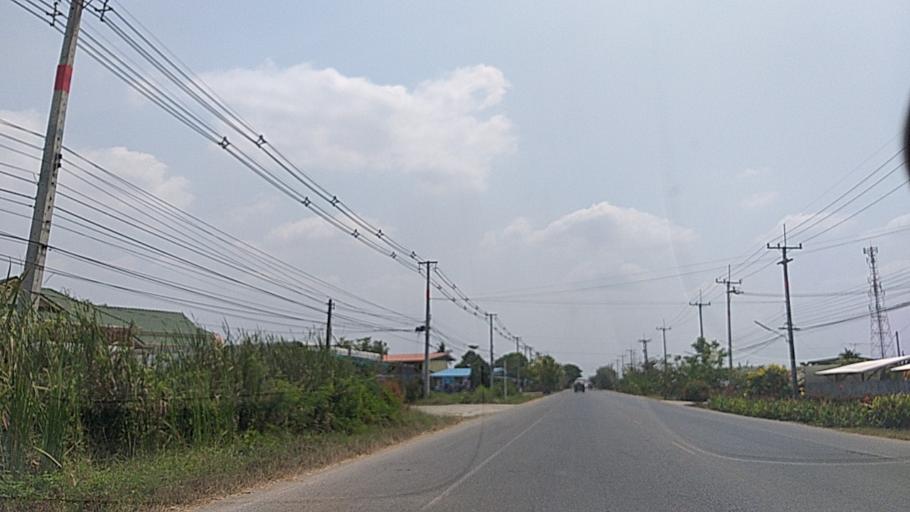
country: TH
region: Chachoengsao
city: Chachoengsao
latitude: 13.7554
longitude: 101.0754
